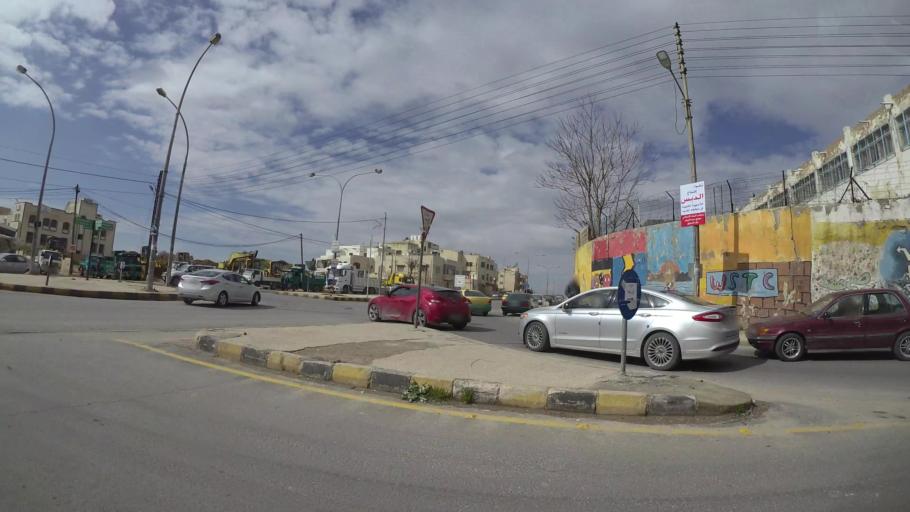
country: JO
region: Amman
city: Wadi as Sir
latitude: 31.9471
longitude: 35.8311
